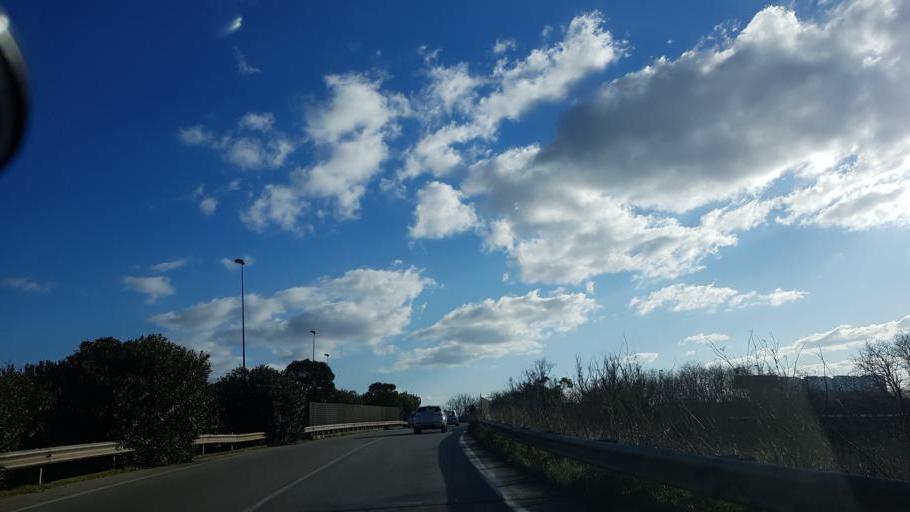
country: IT
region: Apulia
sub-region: Provincia di Brindisi
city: Brindisi
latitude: 40.6321
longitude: 17.9183
